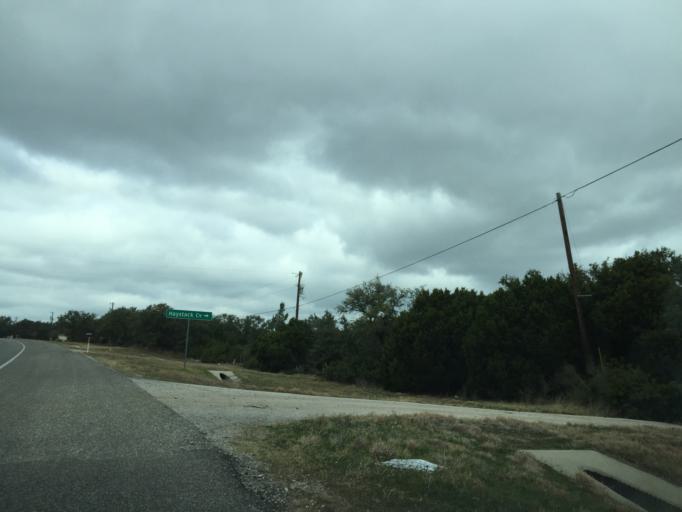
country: US
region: Texas
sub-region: Travis County
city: Briarcliff
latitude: 30.3471
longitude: -98.0515
